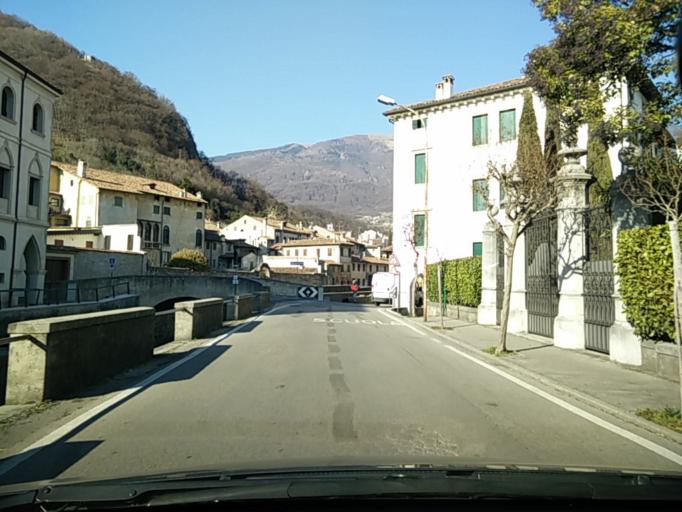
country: IT
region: Veneto
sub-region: Provincia di Treviso
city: Vittorio Veneto
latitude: 45.9978
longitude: 12.2917
